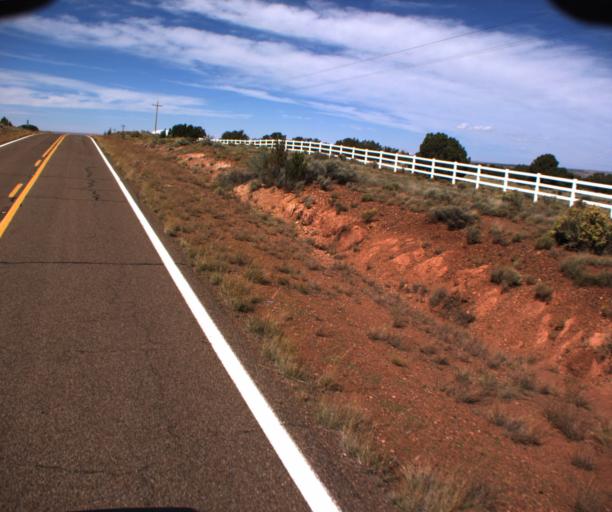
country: US
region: Arizona
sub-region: Apache County
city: Saint Johns
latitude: 34.5812
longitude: -109.6408
